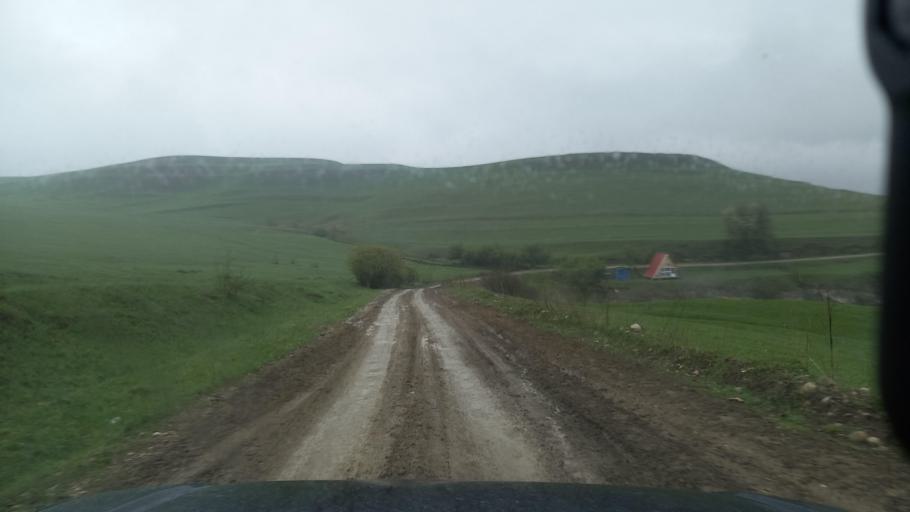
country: RU
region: Kabardino-Balkariya
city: Gundelen
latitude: 43.5935
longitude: 43.1225
